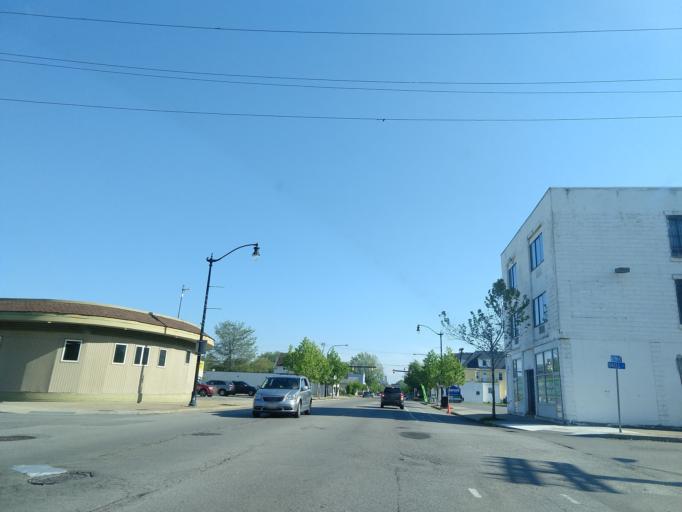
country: US
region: New York
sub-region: Erie County
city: Lackawanna
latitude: 42.8382
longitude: -78.8239
